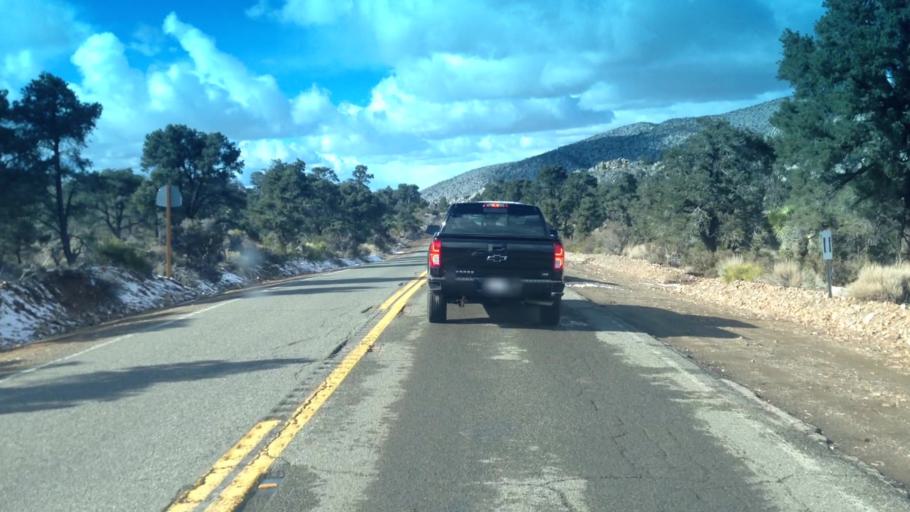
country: US
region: California
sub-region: San Bernardino County
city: Big Bear City
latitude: 34.3115
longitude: -116.8083
